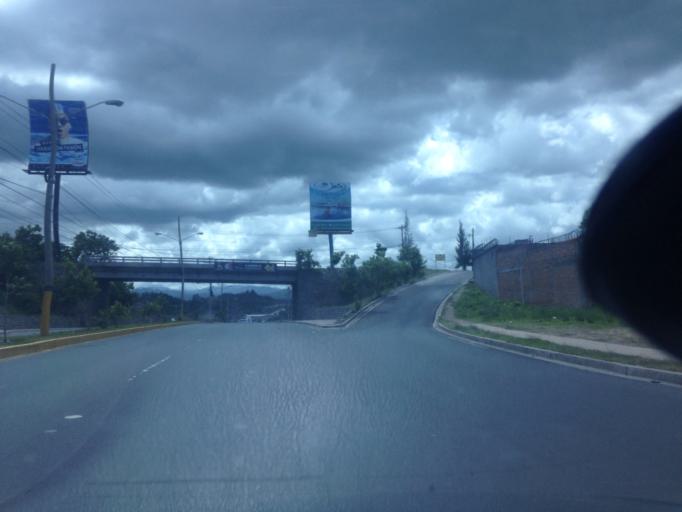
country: HN
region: Francisco Morazan
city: Yaguacire
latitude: 14.0418
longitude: -87.2350
